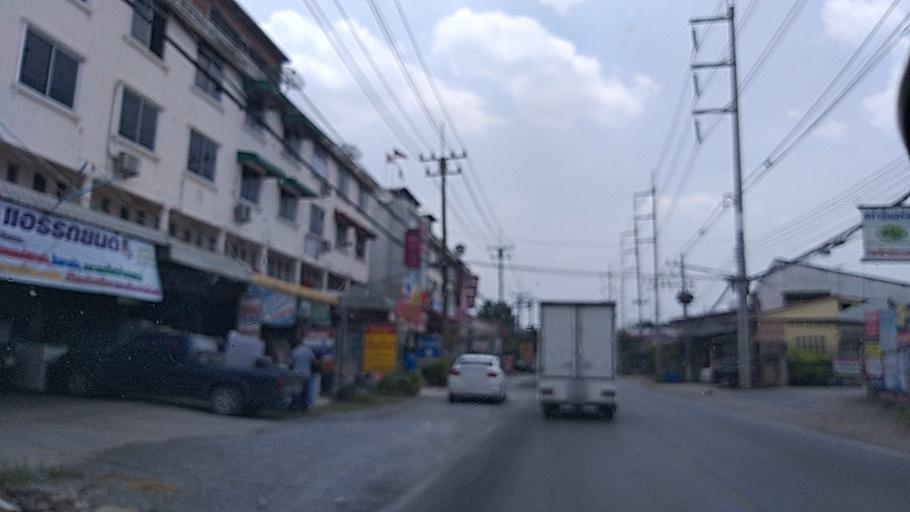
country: TH
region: Bangkok
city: Thawi Watthana
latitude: 13.7540
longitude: 100.2818
